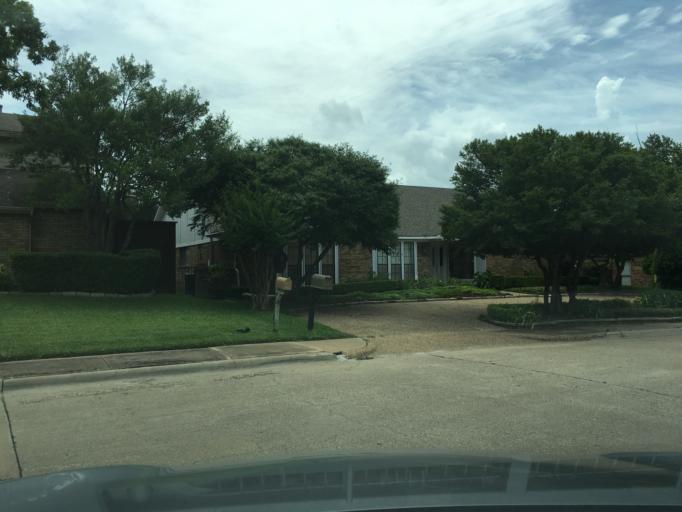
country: US
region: Texas
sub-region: Dallas County
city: Richardson
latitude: 32.9112
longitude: -96.7153
